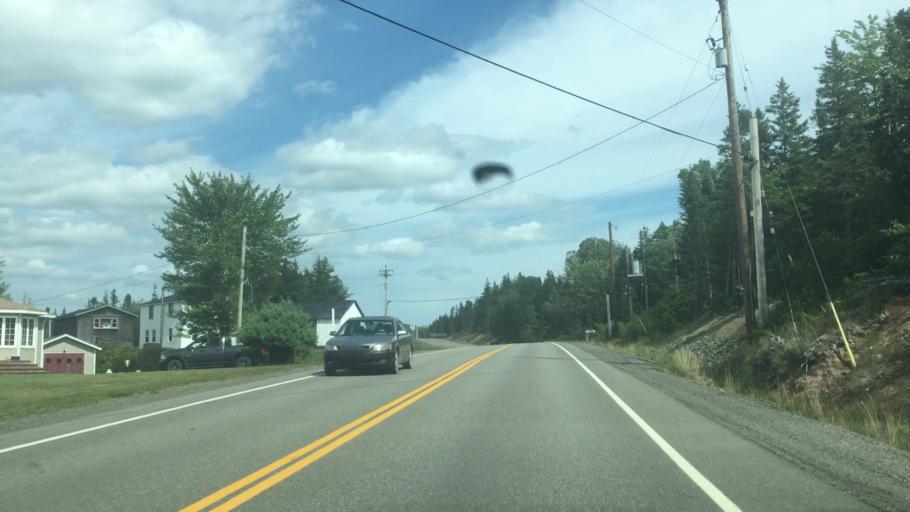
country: CA
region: Nova Scotia
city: Sydney Mines
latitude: 46.3280
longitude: -60.6043
